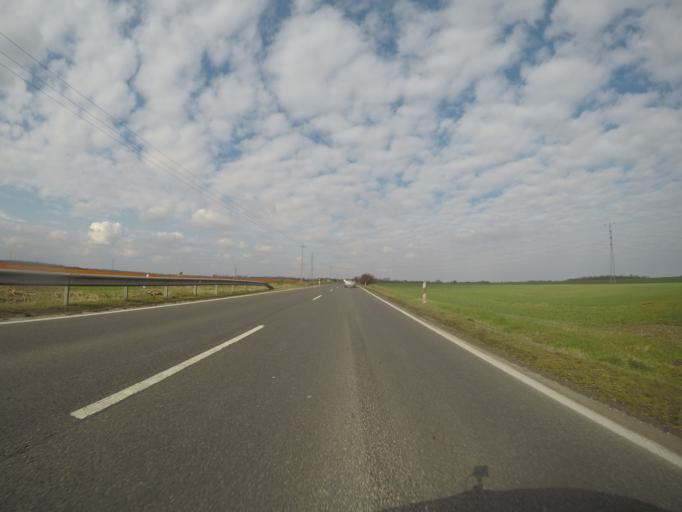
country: HU
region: Tolna
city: Dunafoldvar
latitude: 46.8432
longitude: 18.9103
